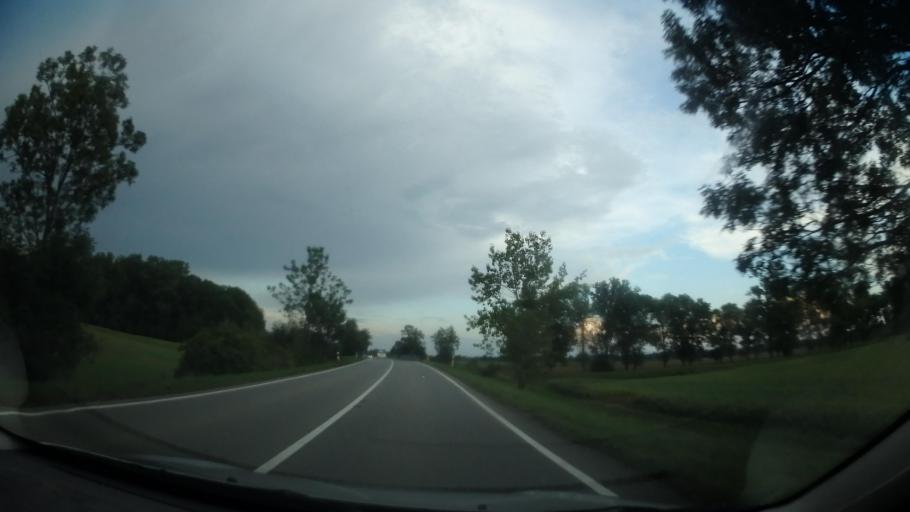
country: CZ
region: Olomoucky
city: Tovacov
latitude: 49.4245
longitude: 17.3144
